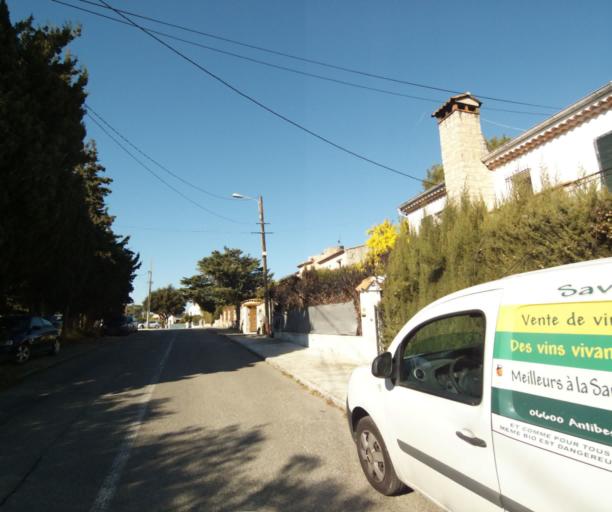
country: FR
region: Provence-Alpes-Cote d'Azur
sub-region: Departement des Alpes-Maritimes
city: Biot
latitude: 43.6084
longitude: 7.0906
